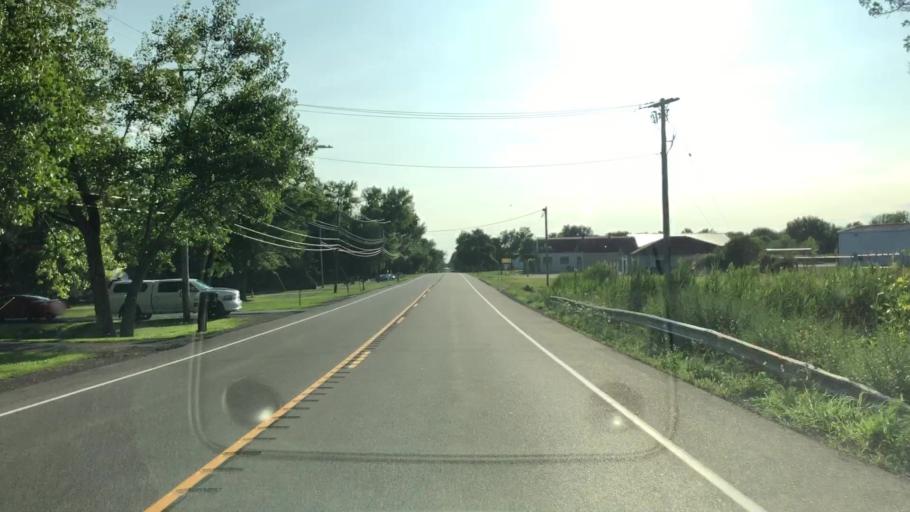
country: US
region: New York
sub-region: Erie County
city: Depew
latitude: 42.8580
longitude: -78.7173
